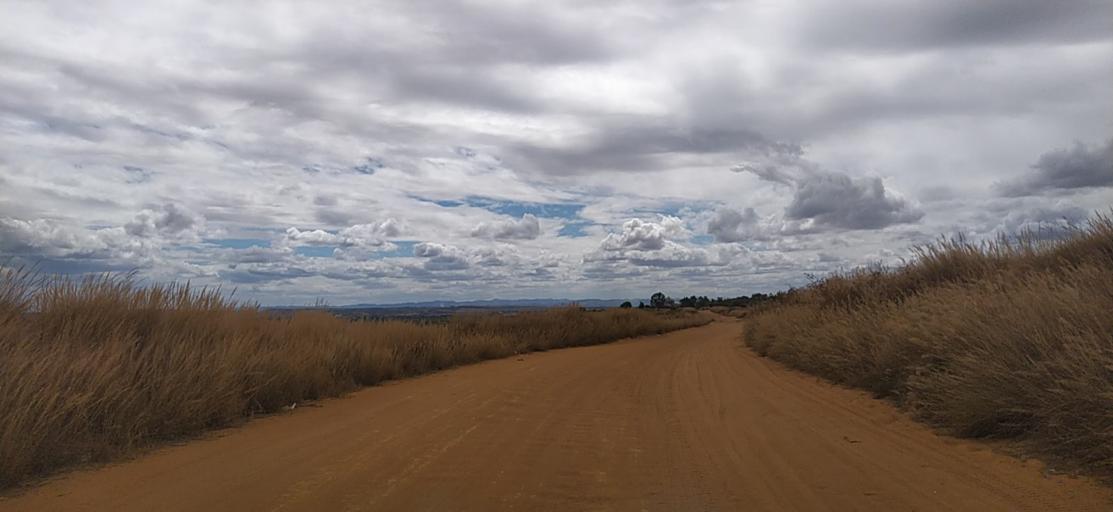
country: MG
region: Alaotra Mangoro
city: Ambatondrazaka
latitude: -17.9046
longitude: 48.2596
